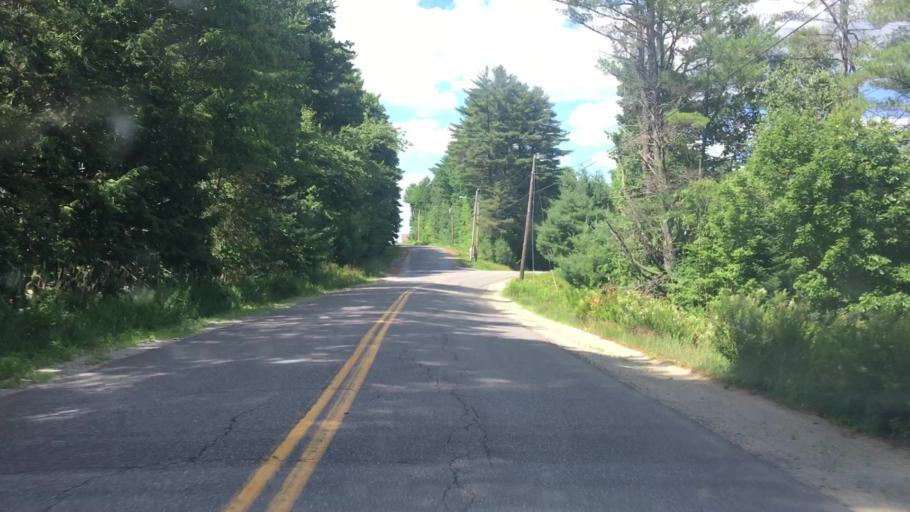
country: US
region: Maine
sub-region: Franklin County
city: Chesterville
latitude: 44.5798
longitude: -70.0904
